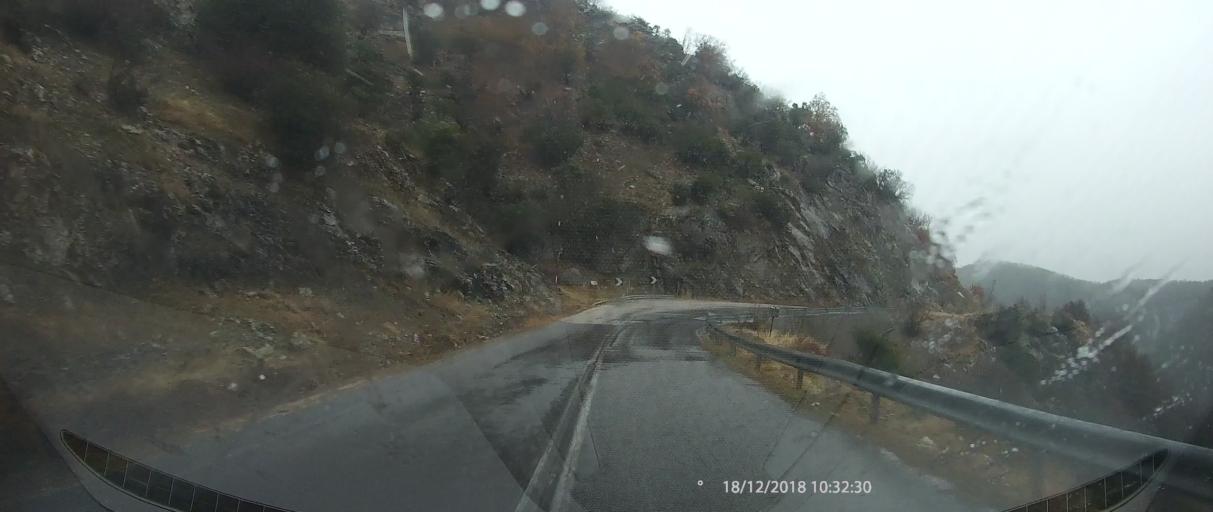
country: GR
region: Central Macedonia
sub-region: Nomos Pierias
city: Kato Milia
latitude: 40.1915
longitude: 22.2925
